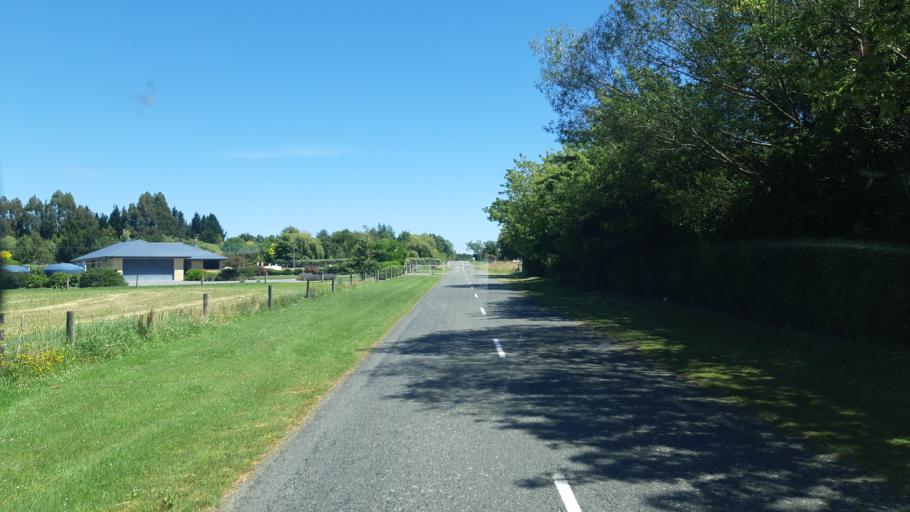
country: NZ
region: Canterbury
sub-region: Timaru District
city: Timaru
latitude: -44.3933
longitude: 171.1429
